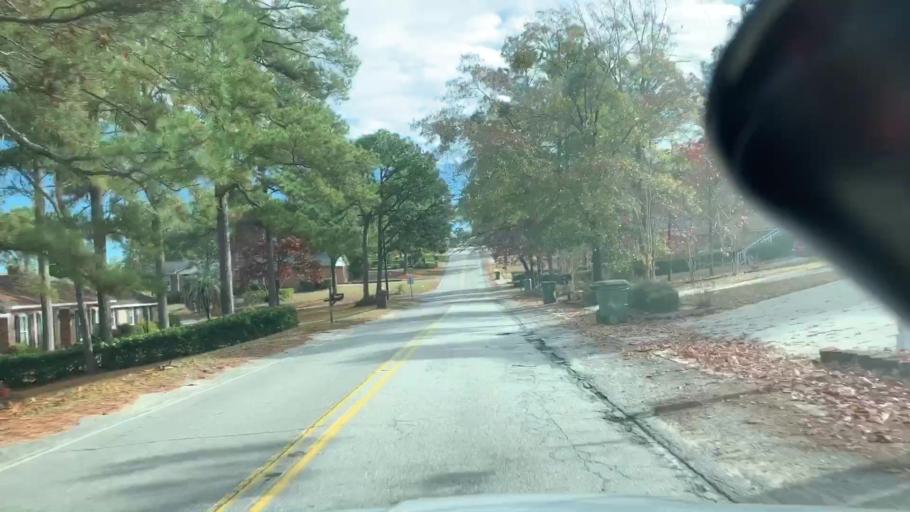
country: US
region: South Carolina
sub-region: Richland County
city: Woodfield
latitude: 34.0639
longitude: -80.9346
